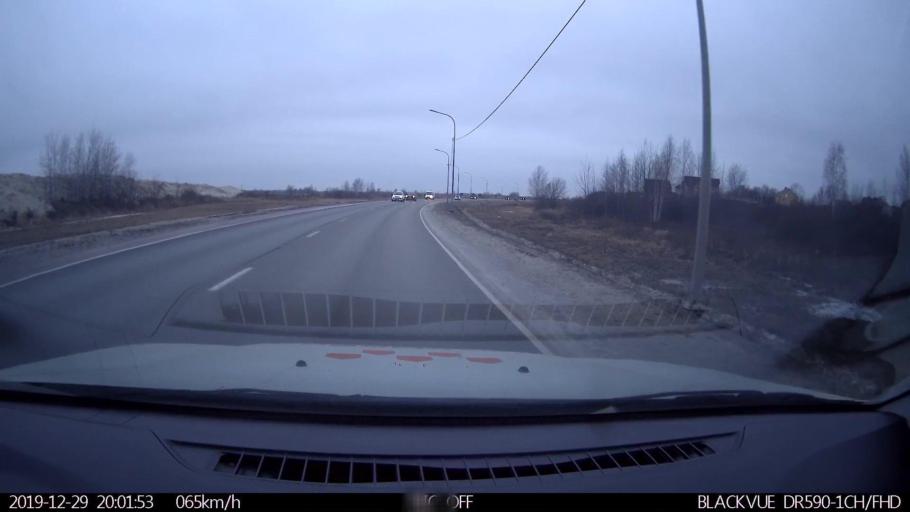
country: RU
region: Nizjnij Novgorod
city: Bor
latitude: 56.3610
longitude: 44.0365
